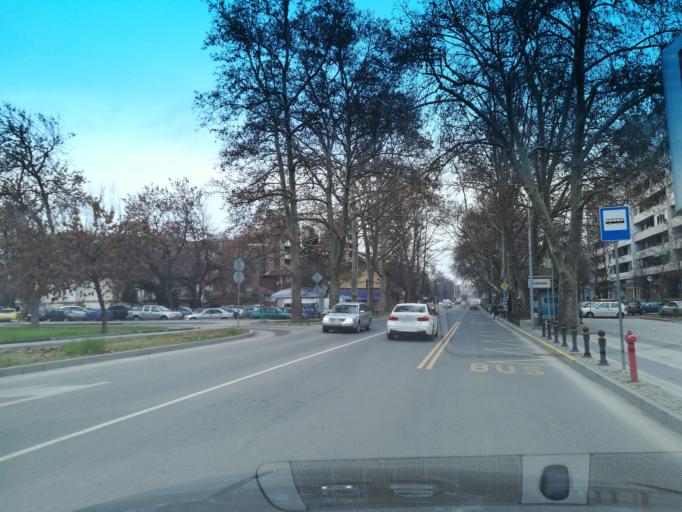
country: BG
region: Plovdiv
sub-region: Obshtina Plovdiv
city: Plovdiv
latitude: 42.1459
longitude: 24.7313
